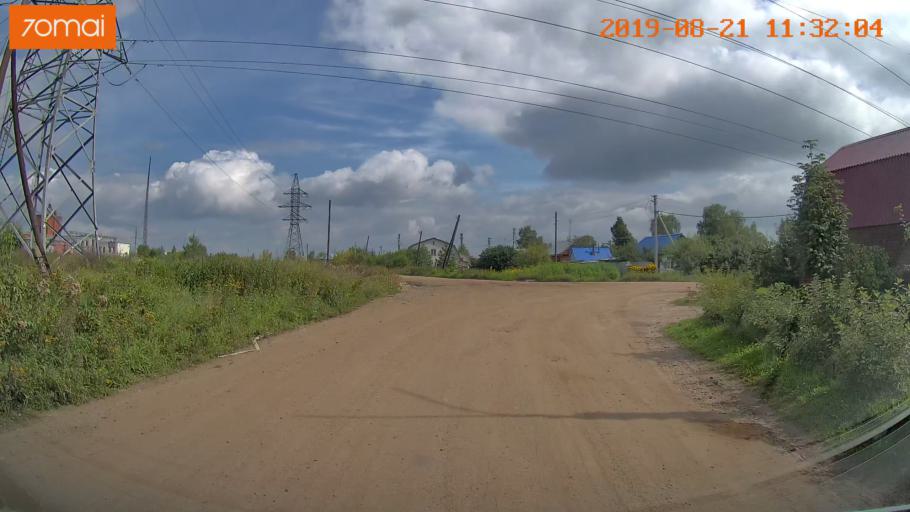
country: RU
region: Ivanovo
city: Novo-Talitsy
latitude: 56.9871
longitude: 40.9097
